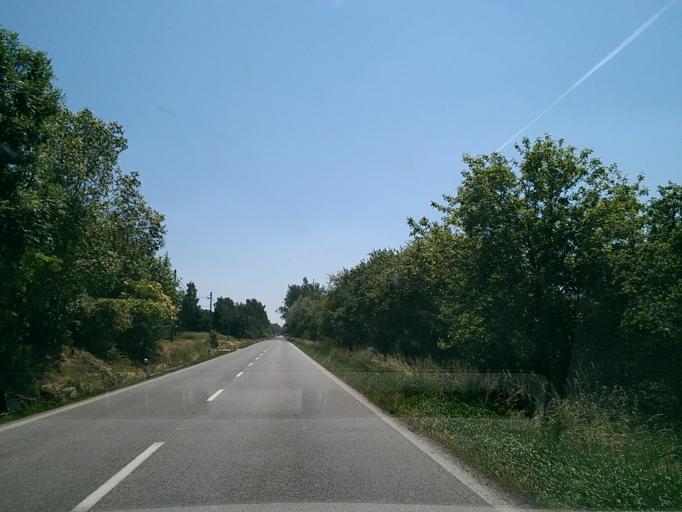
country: CZ
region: Liberecky
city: Rovensko pod Troskami
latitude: 50.5415
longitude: 15.2253
